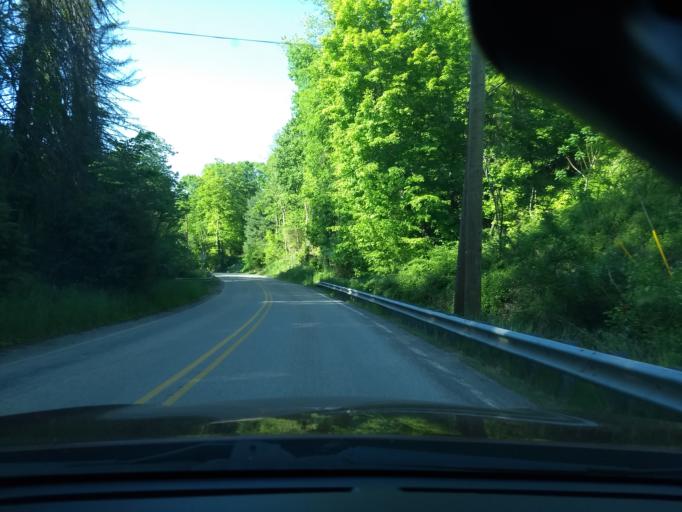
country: US
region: Pennsylvania
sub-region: Allegheny County
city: Versailles
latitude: 40.3001
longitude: -79.8420
